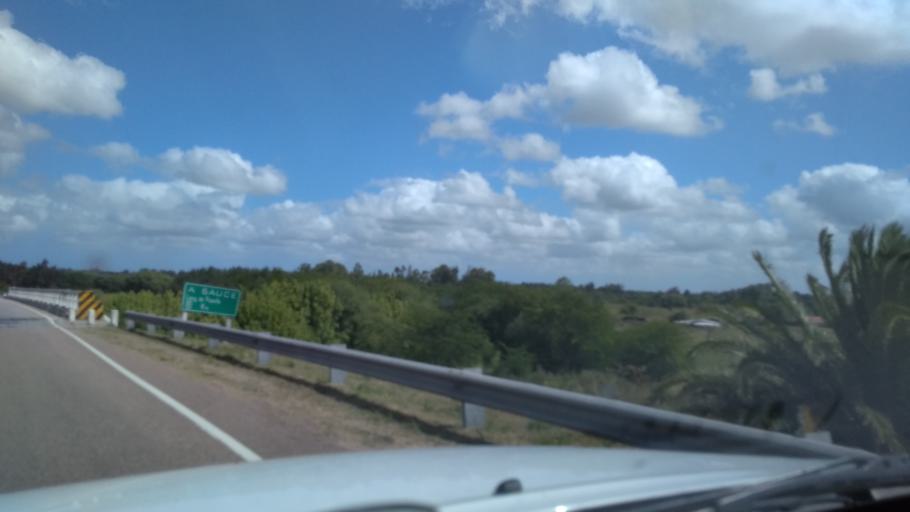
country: UY
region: Canelones
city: Sauce
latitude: -34.6403
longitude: -56.0525
